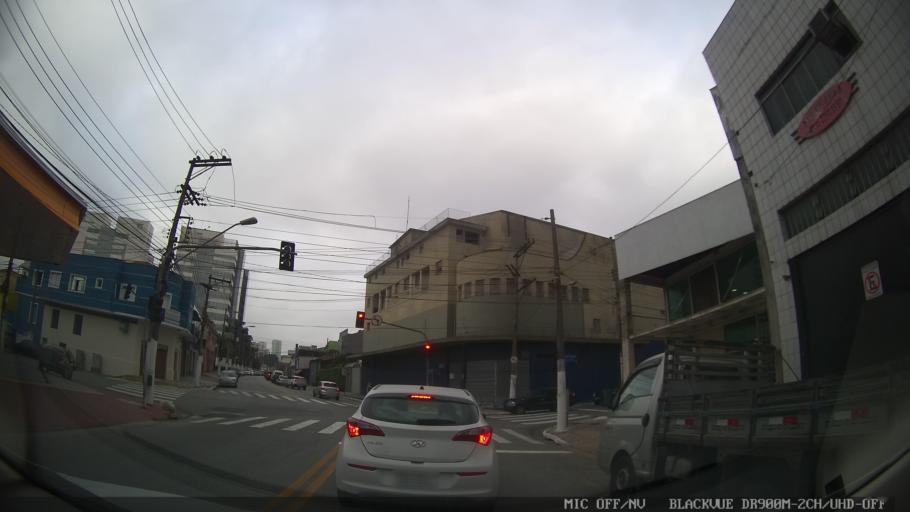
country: BR
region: Sao Paulo
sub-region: Sao Paulo
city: Sao Paulo
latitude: -23.5000
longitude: -46.6125
